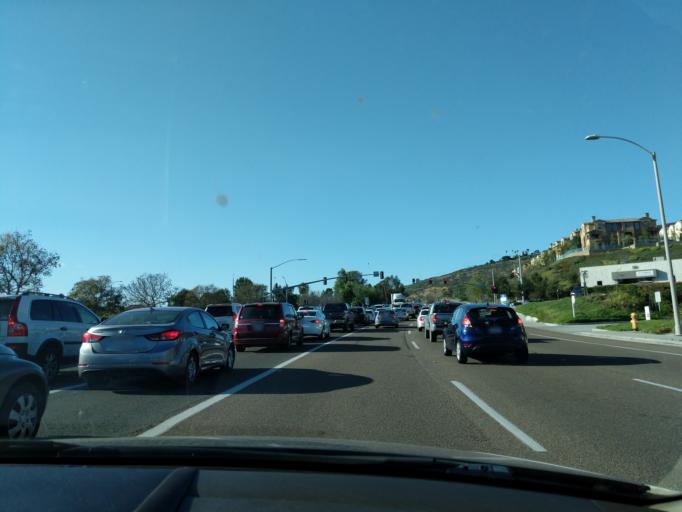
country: US
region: California
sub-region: San Diego County
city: Lake San Marcos
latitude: 33.1061
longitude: -117.2254
